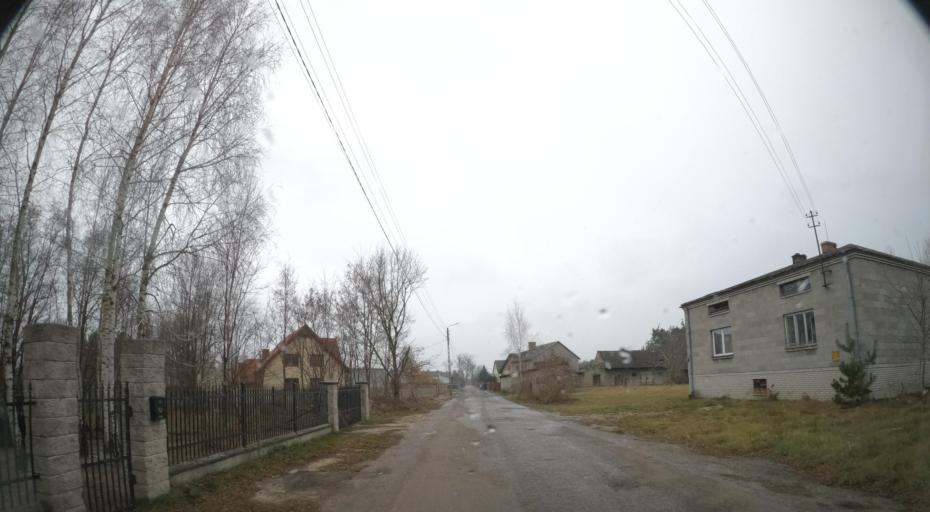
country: PL
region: Masovian Voivodeship
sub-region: Powiat radomski
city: Jedlnia-Letnisko
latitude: 51.3987
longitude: 21.2737
